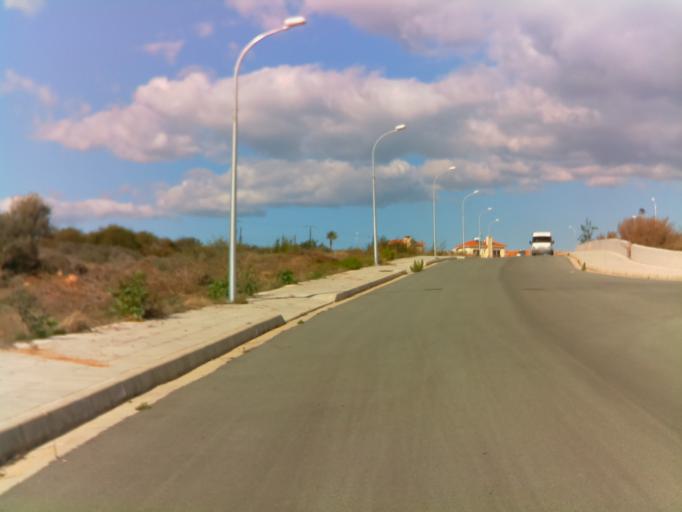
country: CY
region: Limassol
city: Pissouri
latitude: 34.6495
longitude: 32.6980
